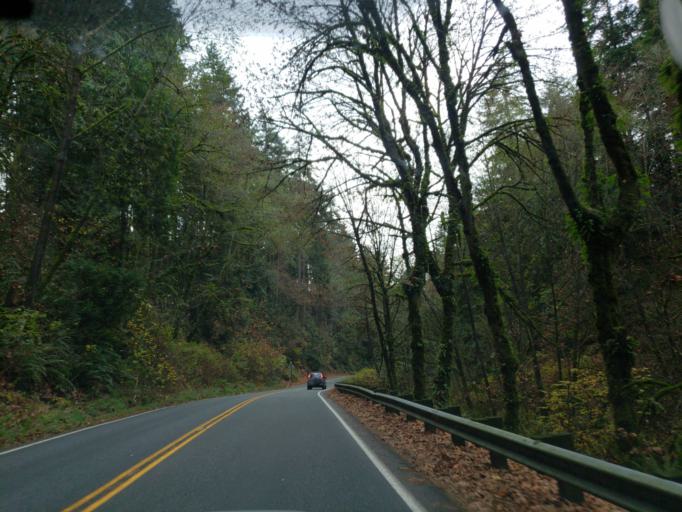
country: US
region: Washington
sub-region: King County
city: Woodinville
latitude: 47.7338
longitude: -122.1358
